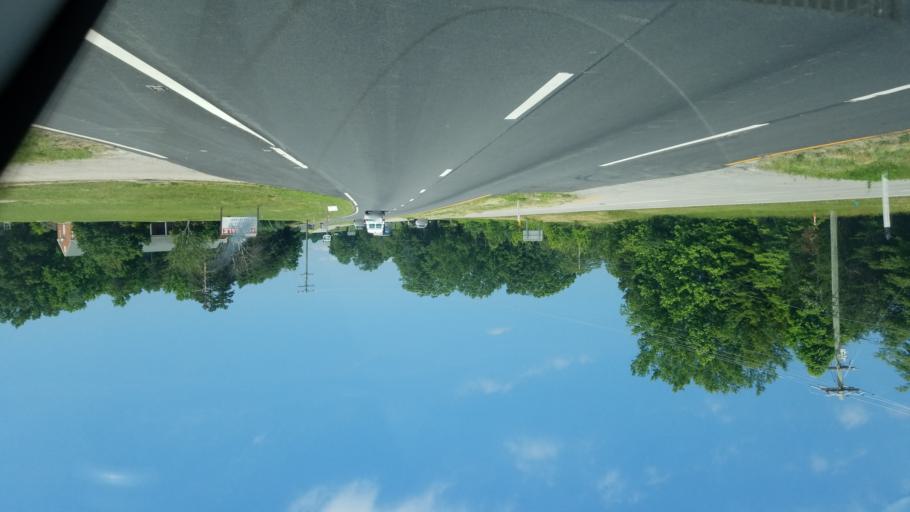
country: US
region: Virginia
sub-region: Pittsylvania County
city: Mount Hermon
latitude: 36.7070
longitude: -79.3731
